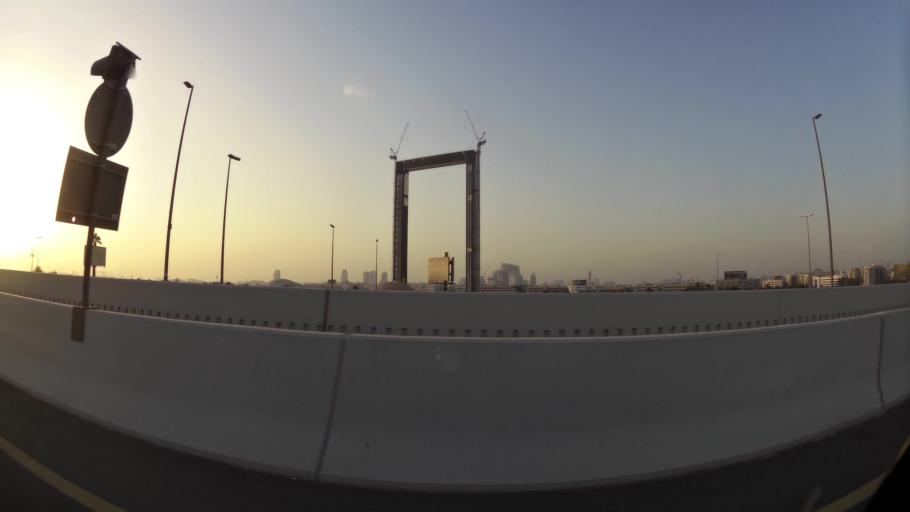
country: AE
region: Ash Shariqah
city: Sharjah
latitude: 25.2314
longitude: 55.3015
